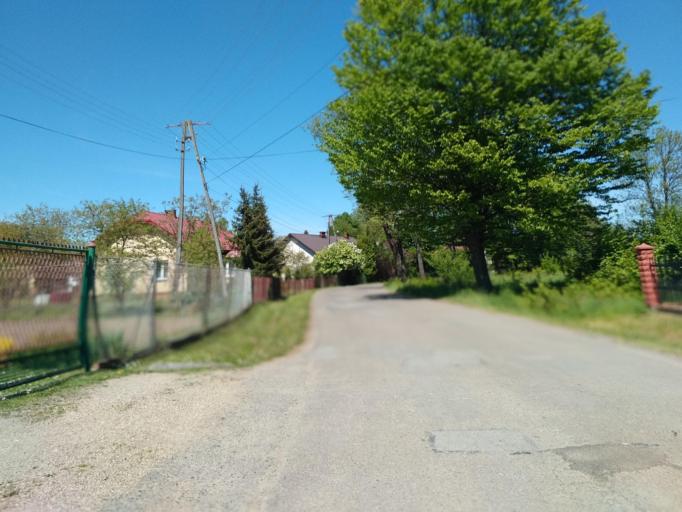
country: PL
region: Subcarpathian Voivodeship
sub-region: Powiat brzozowski
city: Gorki
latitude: 49.6512
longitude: 22.0315
